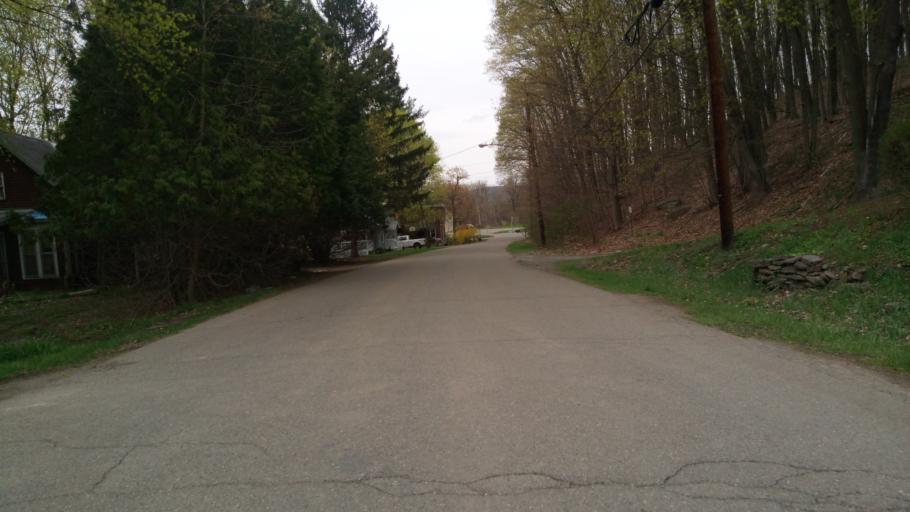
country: US
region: New York
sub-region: Chemung County
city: Southport
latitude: 42.0148
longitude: -76.7261
